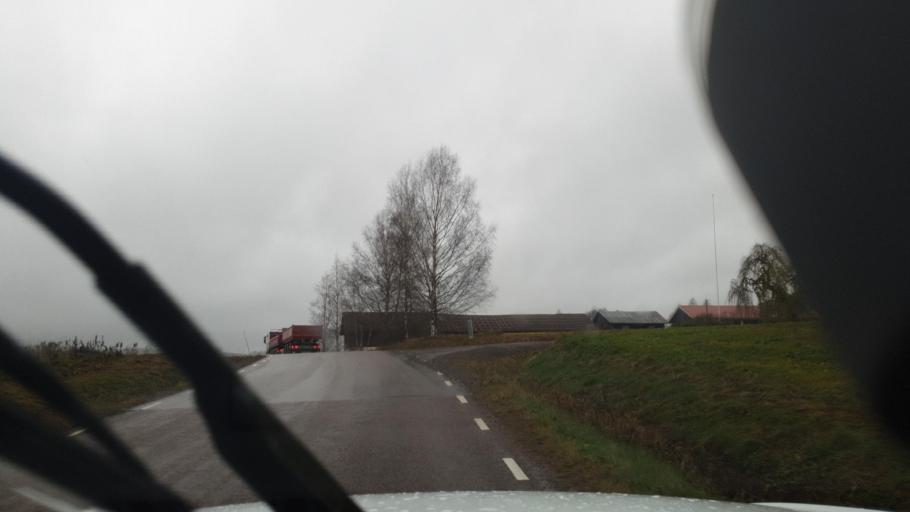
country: SE
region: Vaermland
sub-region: Sunne Kommun
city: Sunne
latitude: 59.7434
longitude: 13.0824
